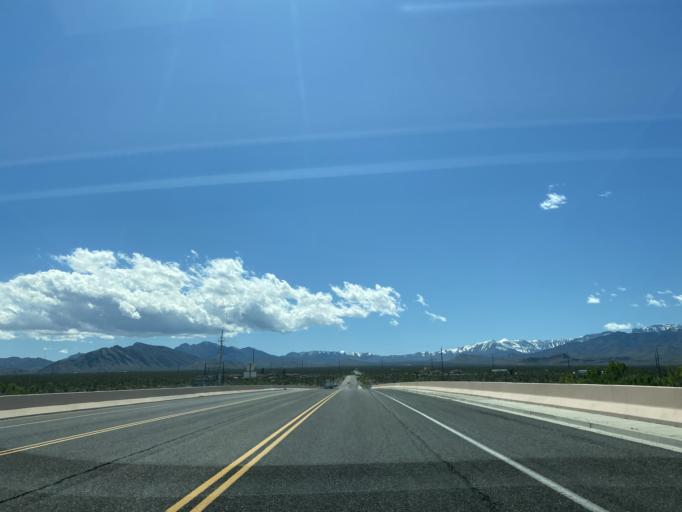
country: US
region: Nevada
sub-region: Clark County
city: Summerlin South
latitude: 36.3611
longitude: -115.3526
